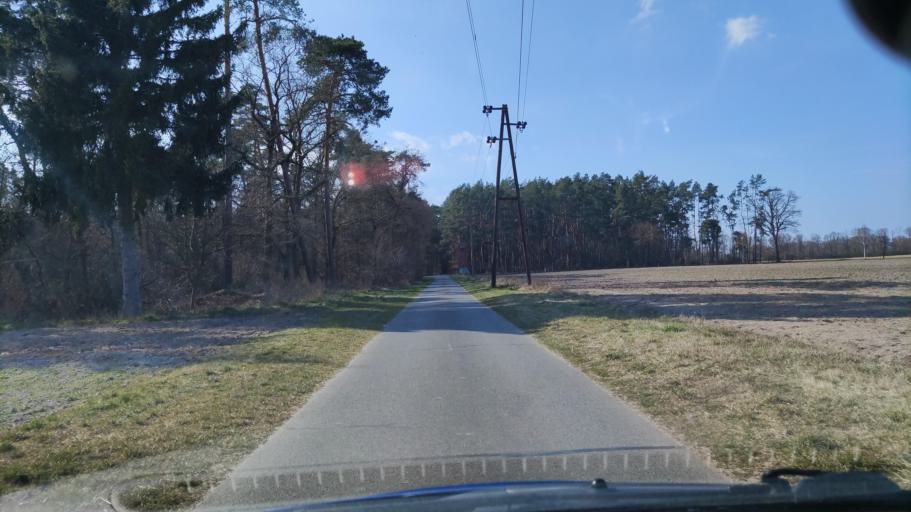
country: DE
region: Lower Saxony
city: Damnatz
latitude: 53.1099
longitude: 11.1627
